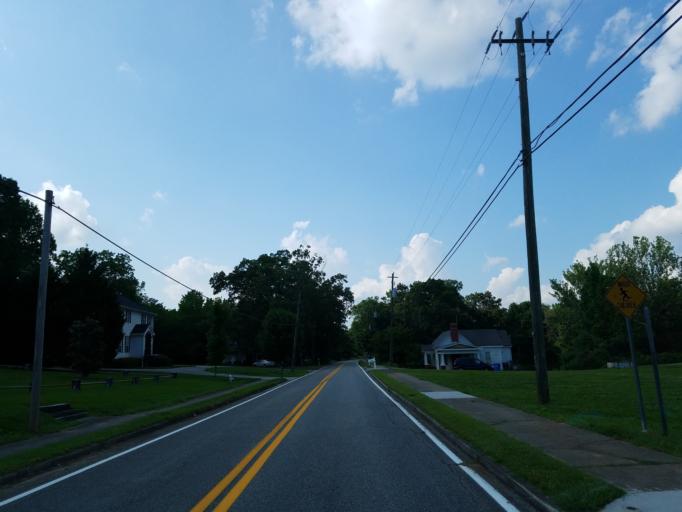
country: US
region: Georgia
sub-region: Cherokee County
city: Ball Ground
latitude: 34.3421
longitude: -84.3774
